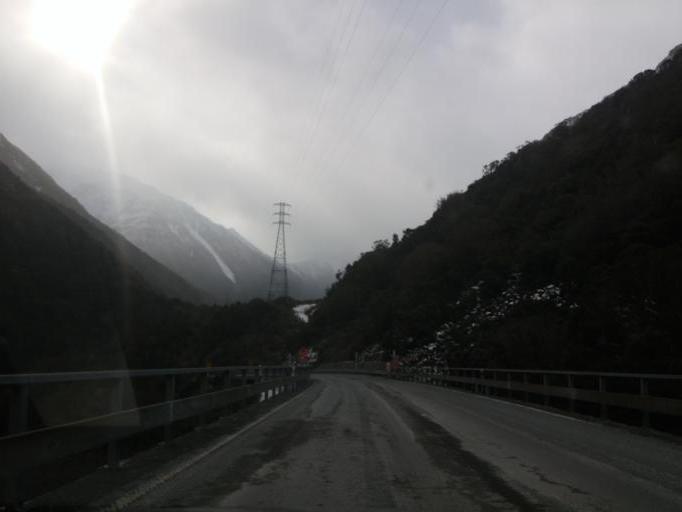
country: NZ
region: West Coast
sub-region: Grey District
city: Greymouth
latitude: -42.8846
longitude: 171.5559
